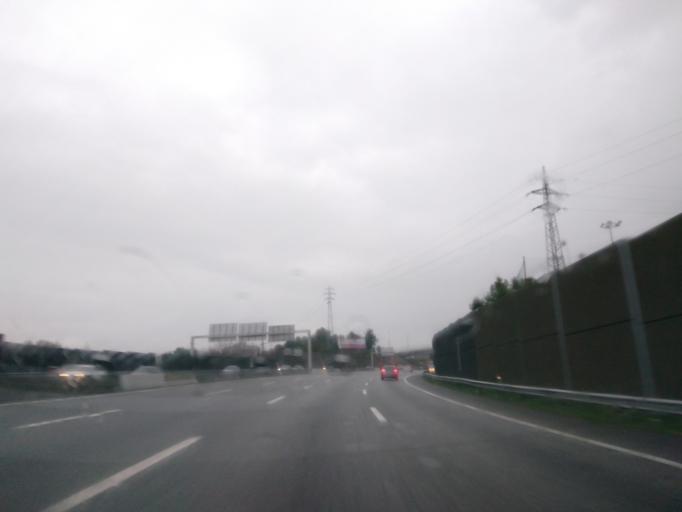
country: PT
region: Porto
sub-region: Maia
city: Pedroucos
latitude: 41.1889
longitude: -8.5947
